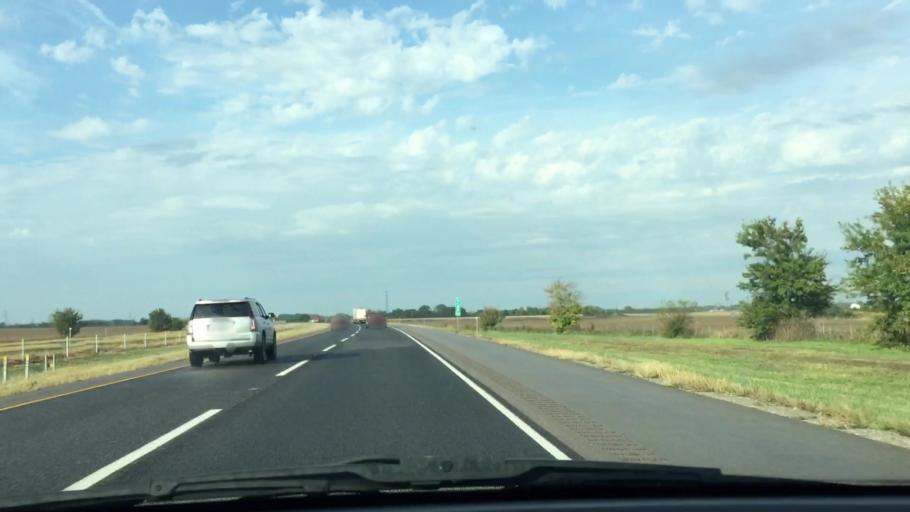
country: US
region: Illinois
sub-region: Lee County
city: Dixon
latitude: 41.7794
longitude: -89.5606
